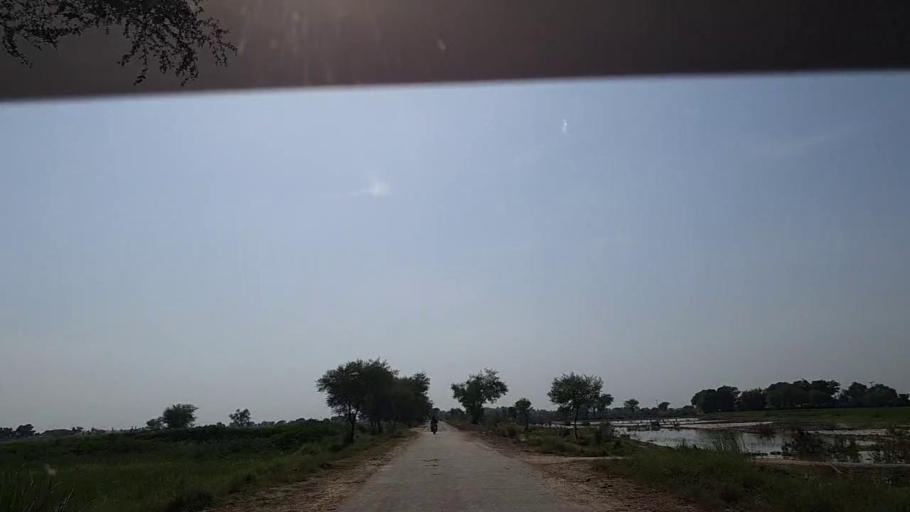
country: PK
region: Sindh
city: Khanpur
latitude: 27.8430
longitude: 69.3843
